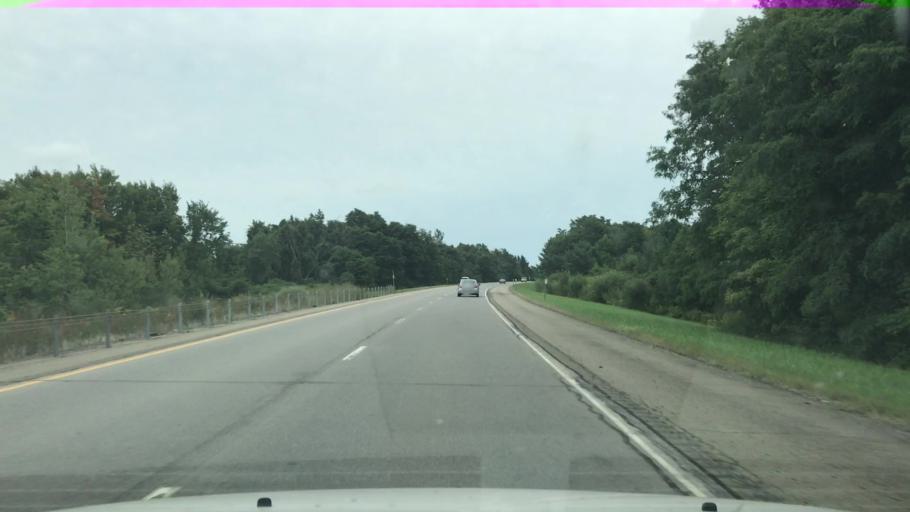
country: US
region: New York
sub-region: Erie County
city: Springville
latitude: 42.5742
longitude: -78.7185
